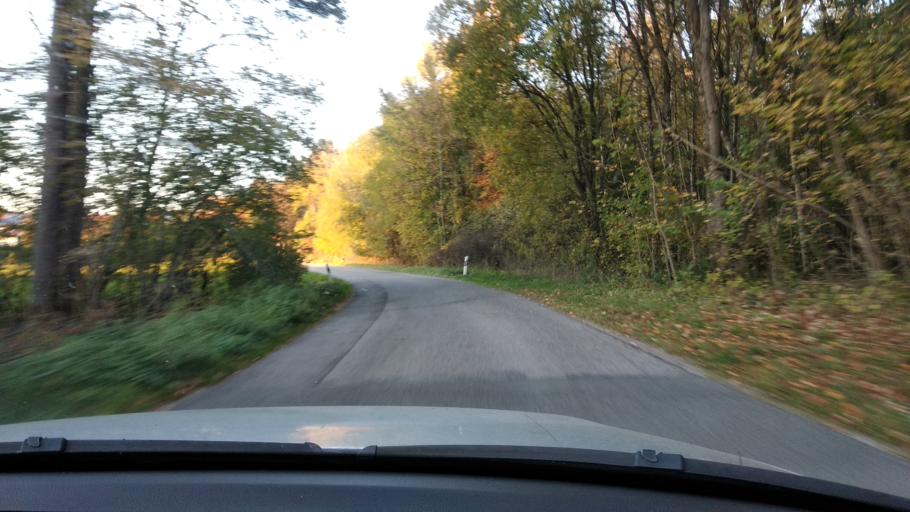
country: DE
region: Bavaria
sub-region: Upper Bavaria
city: Egmating
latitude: 47.9965
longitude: 11.8003
